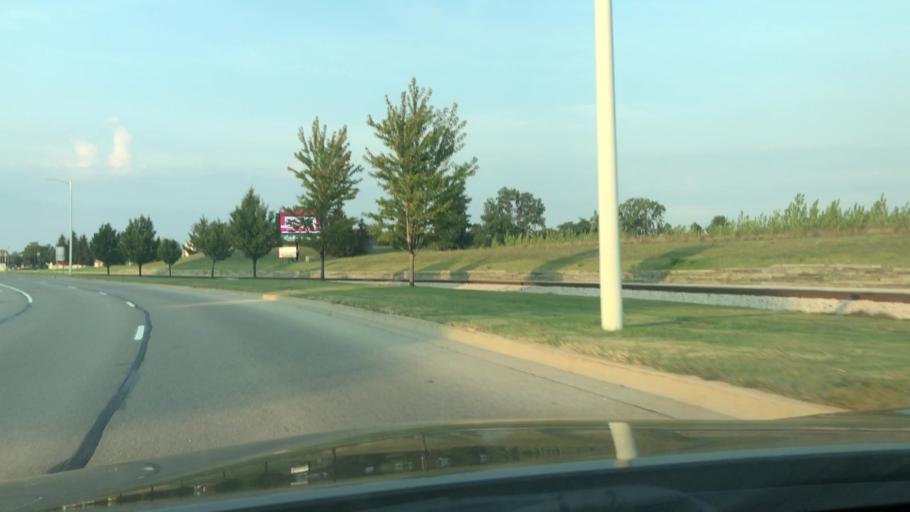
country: US
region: Michigan
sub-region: Muskegon County
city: Muskegon
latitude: 43.2399
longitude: -86.2533
